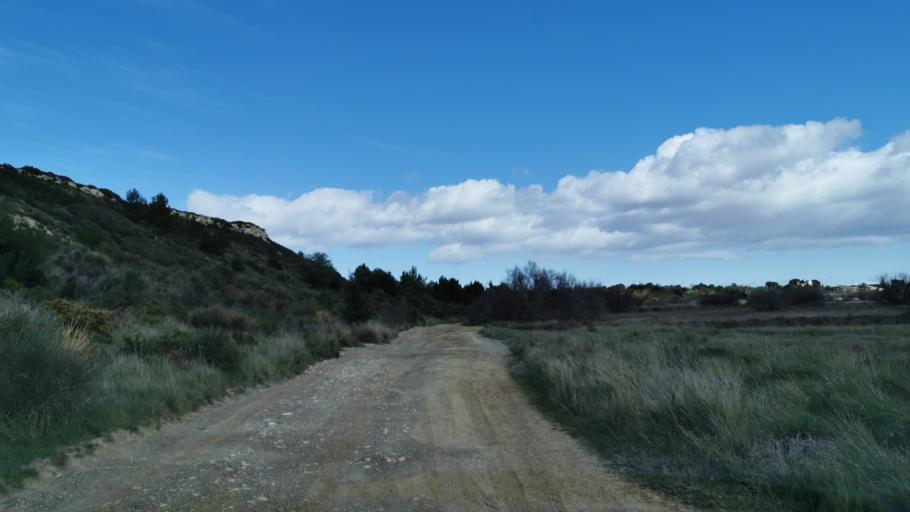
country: FR
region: Languedoc-Roussillon
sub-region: Departement de l'Aude
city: Narbonne
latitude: 43.1480
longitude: 2.9860
